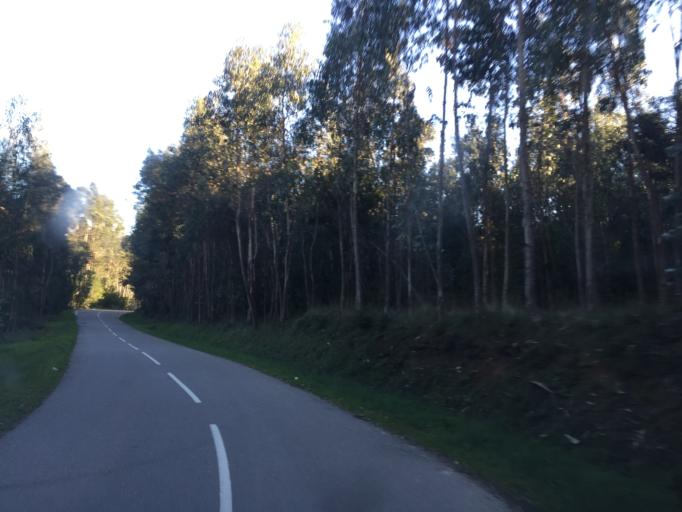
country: PT
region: Coimbra
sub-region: Figueira da Foz
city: Alhadas
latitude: 40.1579
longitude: -8.8006
